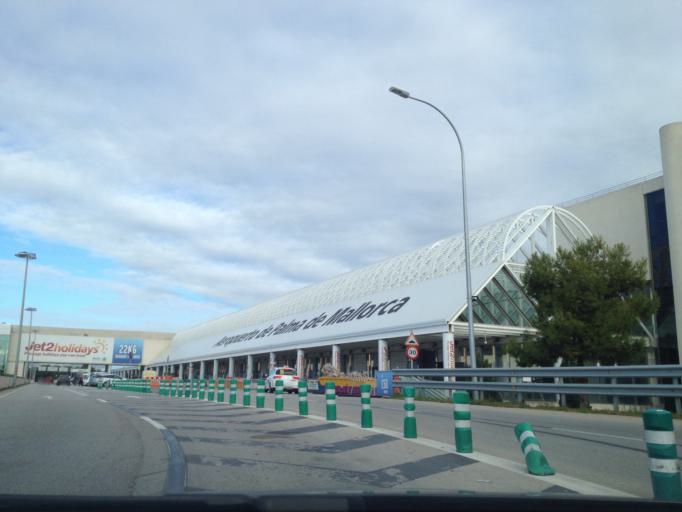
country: ES
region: Balearic Islands
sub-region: Illes Balears
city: s'Arenal
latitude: 39.5460
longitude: 2.7313
